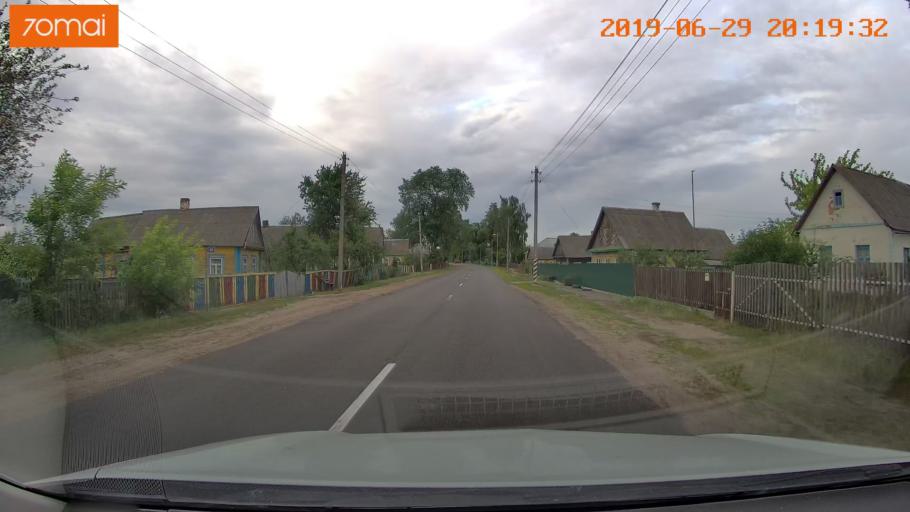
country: BY
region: Brest
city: Asnyezhytsy
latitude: 52.4022
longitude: 26.2447
